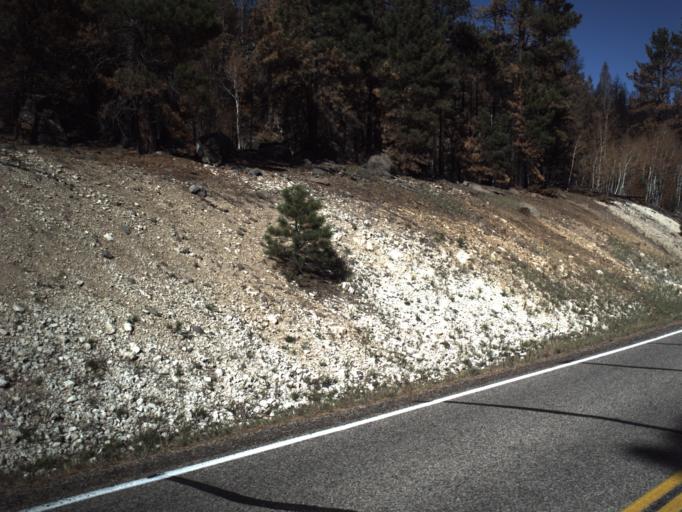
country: US
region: Utah
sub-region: Iron County
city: Parowan
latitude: 37.6547
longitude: -112.6807
